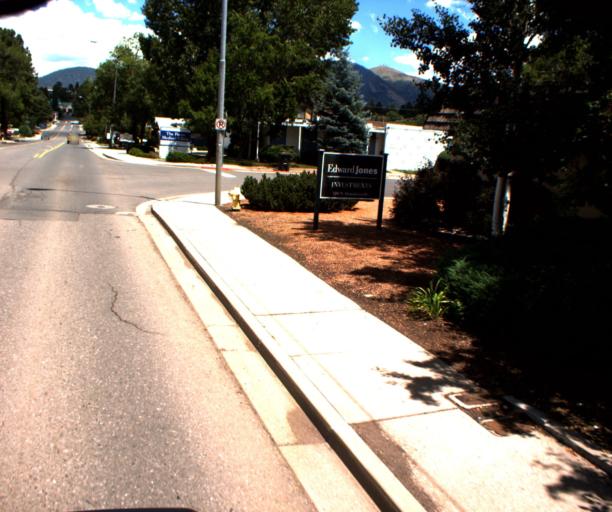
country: US
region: Arizona
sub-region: Coconino County
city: Flagstaff
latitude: 35.2035
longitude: -111.6488
